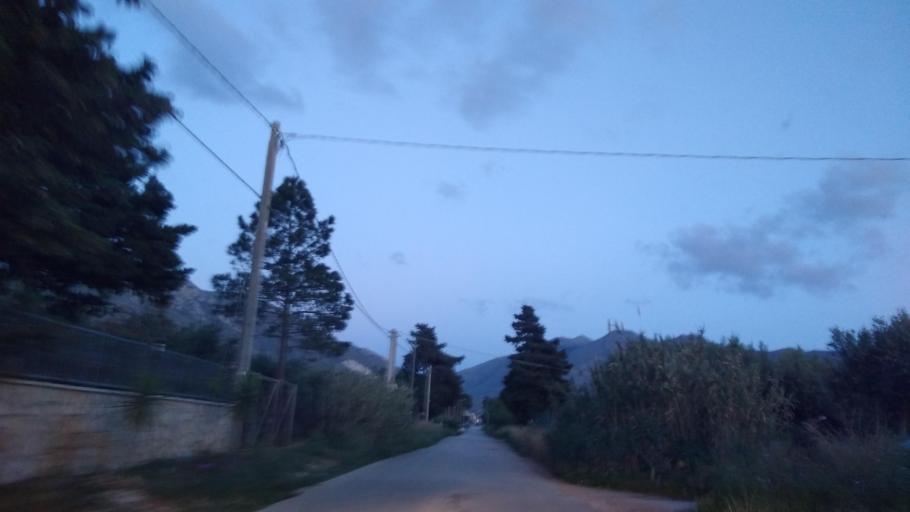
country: IT
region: Sicily
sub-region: Trapani
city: Castelluzzo
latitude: 38.1063
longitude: 12.7296
